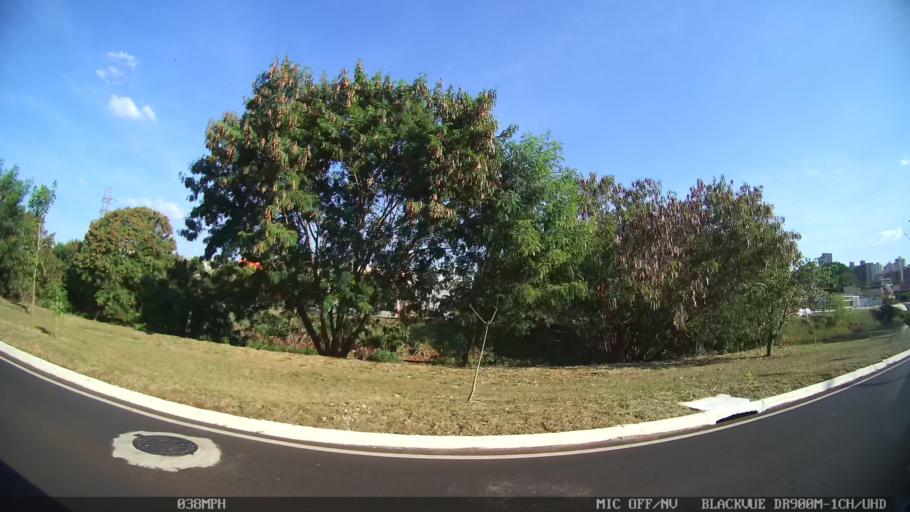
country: BR
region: Sao Paulo
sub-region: Ribeirao Preto
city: Ribeirao Preto
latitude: -21.2093
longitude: -47.7858
